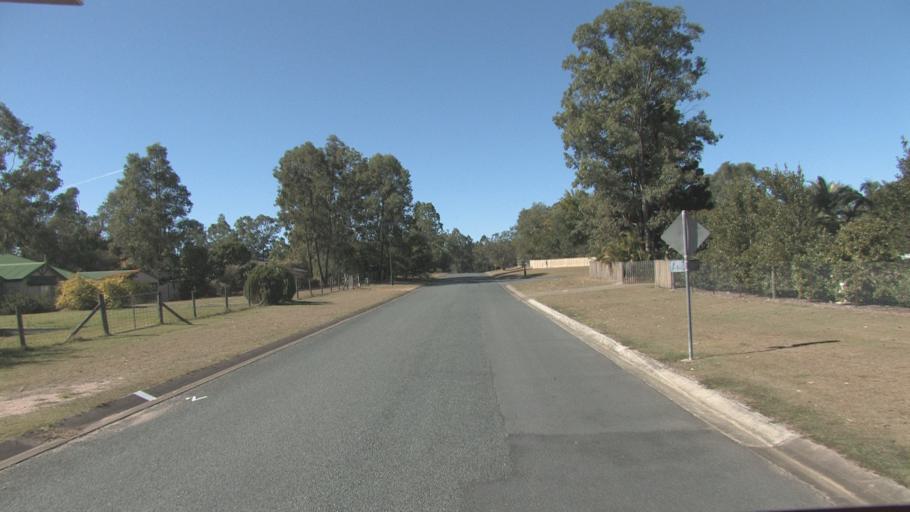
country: AU
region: Queensland
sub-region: Logan
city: North Maclean
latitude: -27.8192
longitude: 152.9498
